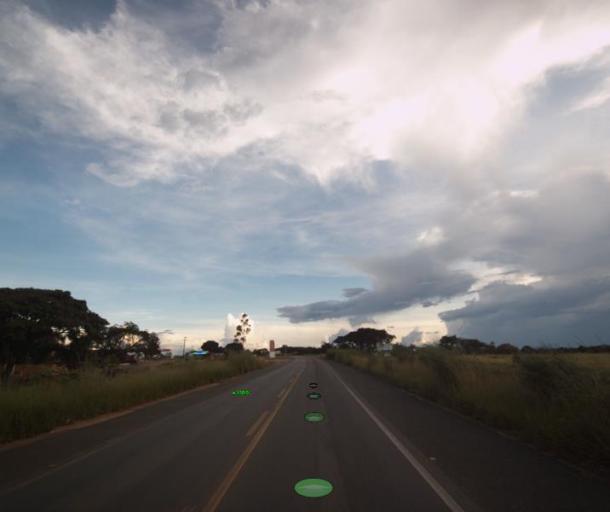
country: BR
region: Goias
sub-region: Uruacu
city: Uruacu
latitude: -14.1599
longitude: -49.1225
